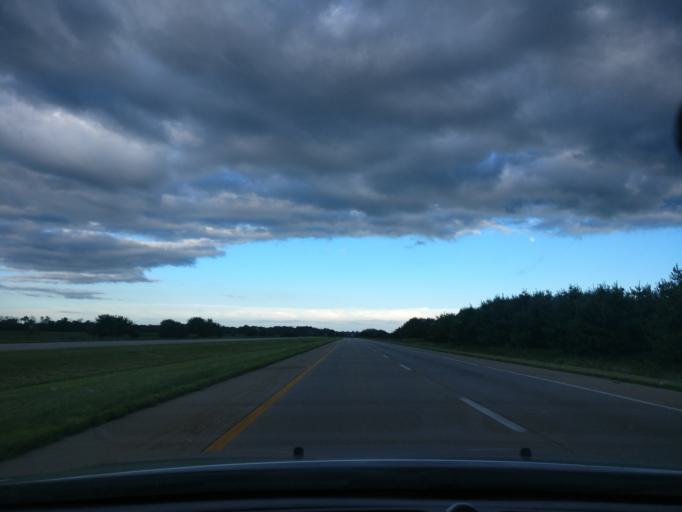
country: US
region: Ohio
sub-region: Greene County
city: Shawnee Hills
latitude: 39.6808
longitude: -83.8294
